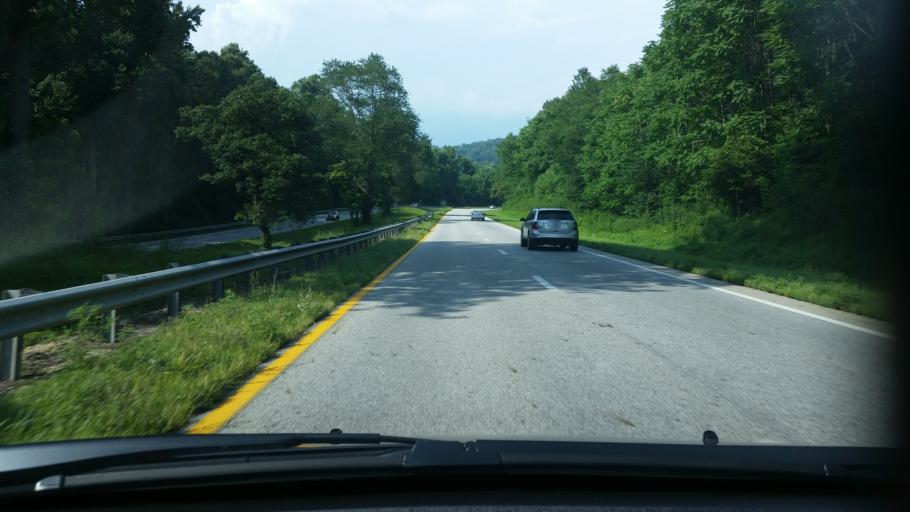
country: US
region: Virginia
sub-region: Nelson County
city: Lovingston
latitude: 37.7359
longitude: -78.8920
